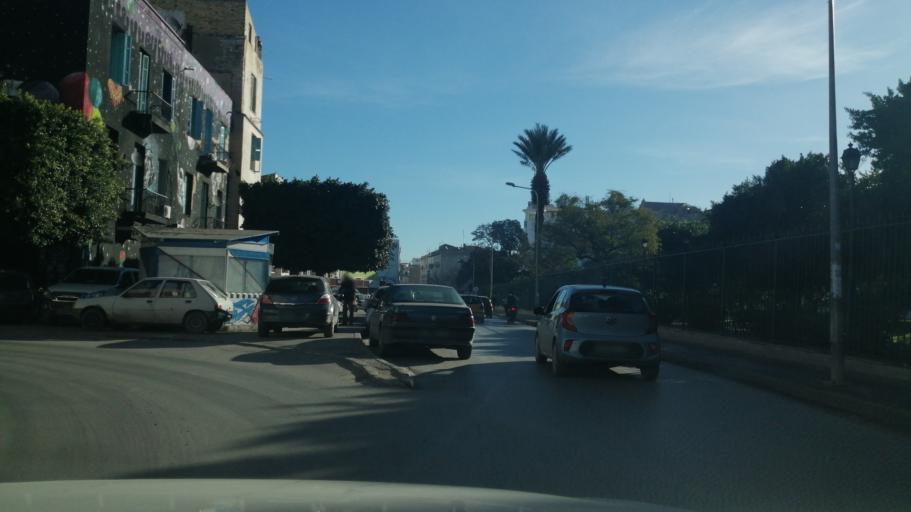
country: TN
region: Tunis
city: Tunis
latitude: 36.8055
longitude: 10.1785
